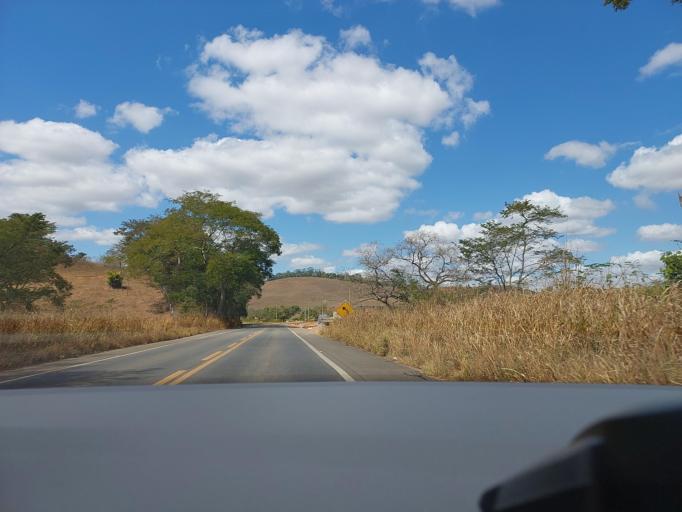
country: BR
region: Minas Gerais
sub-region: Muriae
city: Muriae
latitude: -21.1479
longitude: -42.1637
